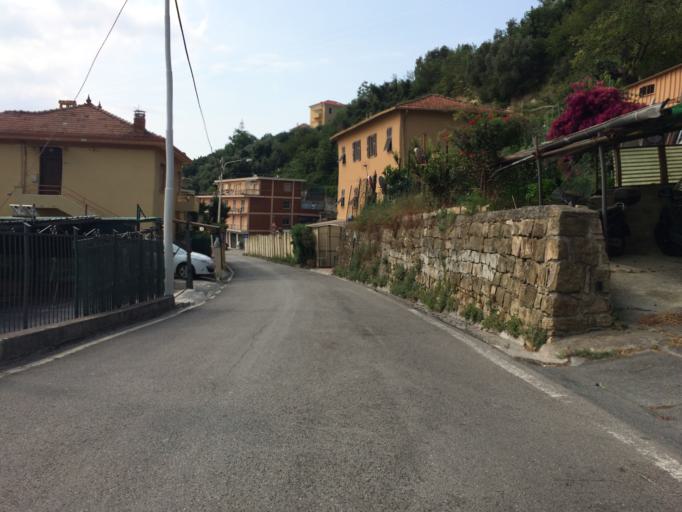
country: IT
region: Liguria
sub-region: Provincia di Imperia
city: San Remo
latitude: 43.8266
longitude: 7.7682
